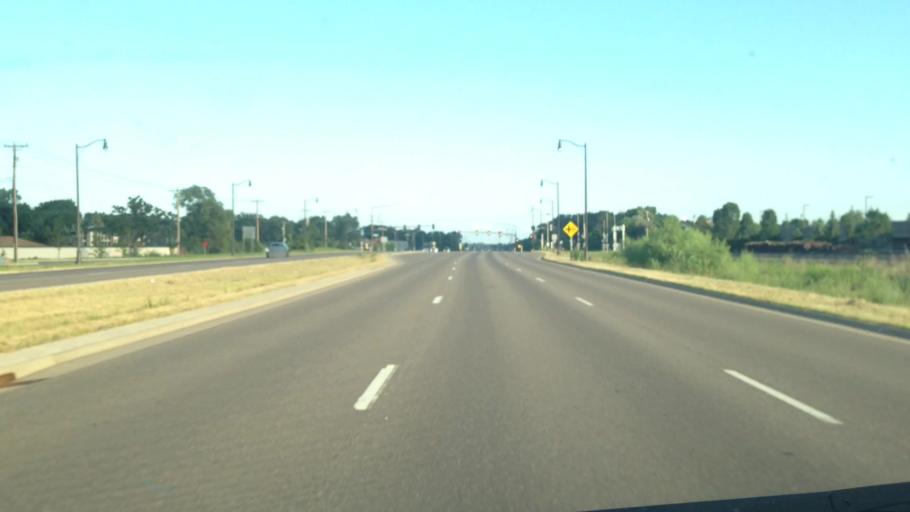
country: US
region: Minnesota
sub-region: Hennepin County
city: Brooklyn Park
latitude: 45.0715
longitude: -93.3696
